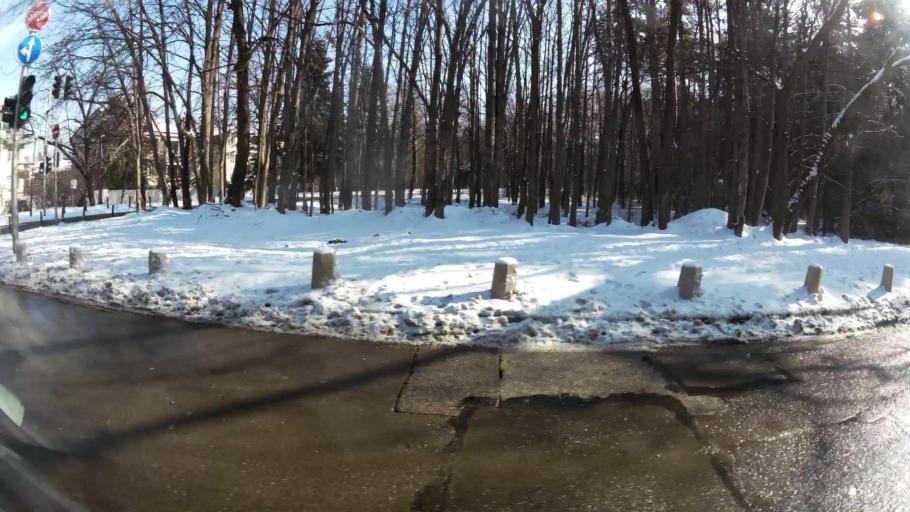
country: BG
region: Sofia-Capital
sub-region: Stolichna Obshtina
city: Sofia
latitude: 42.6662
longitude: 23.3139
